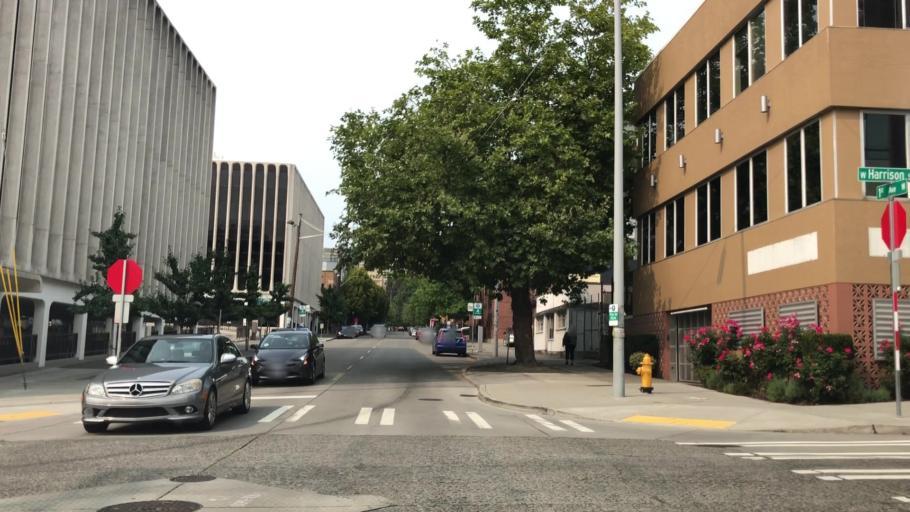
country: US
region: Washington
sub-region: King County
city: Seattle
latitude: 47.6220
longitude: -122.3580
